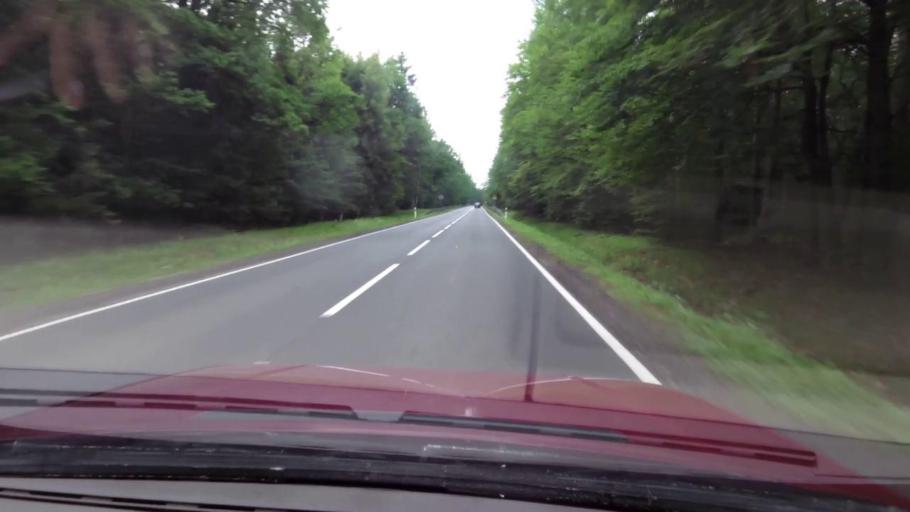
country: PL
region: Pomeranian Voivodeship
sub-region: Powiat bytowski
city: Trzebielino
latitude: 54.2266
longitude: 17.0870
